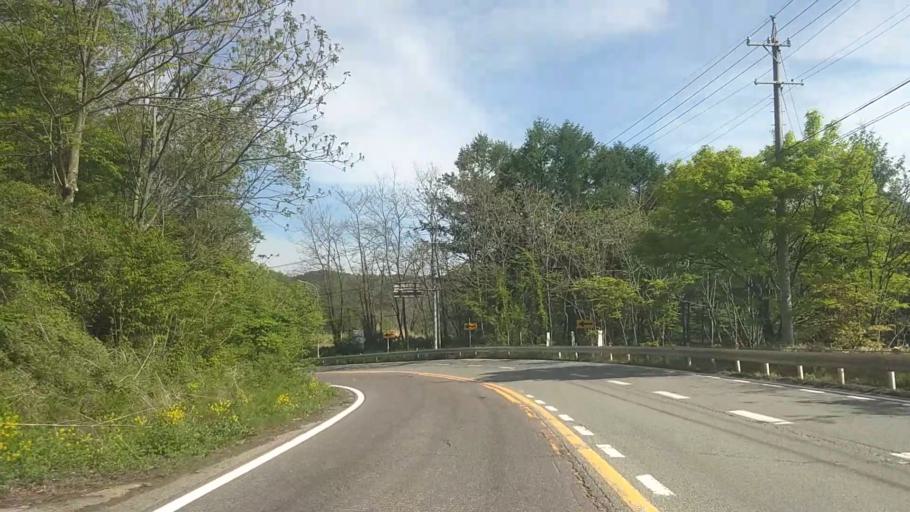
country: JP
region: Nagano
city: Saku
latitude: 36.0055
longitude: 138.5026
